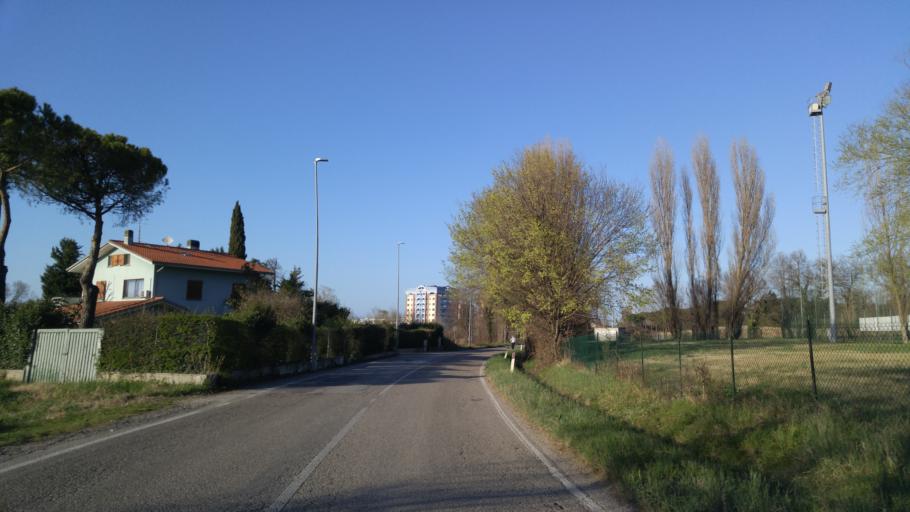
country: IT
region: The Marches
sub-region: Provincia di Pesaro e Urbino
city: Pesaro
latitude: 43.8844
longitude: 12.9070
